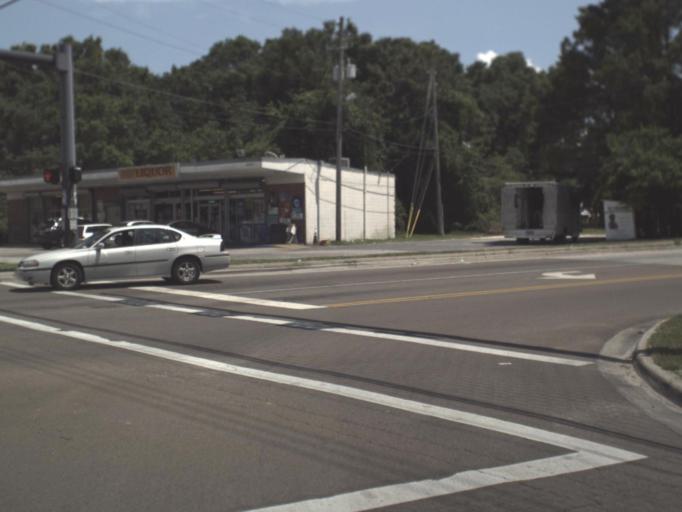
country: US
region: Florida
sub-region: Alachua County
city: Gainesville
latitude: 29.6454
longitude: -82.2945
